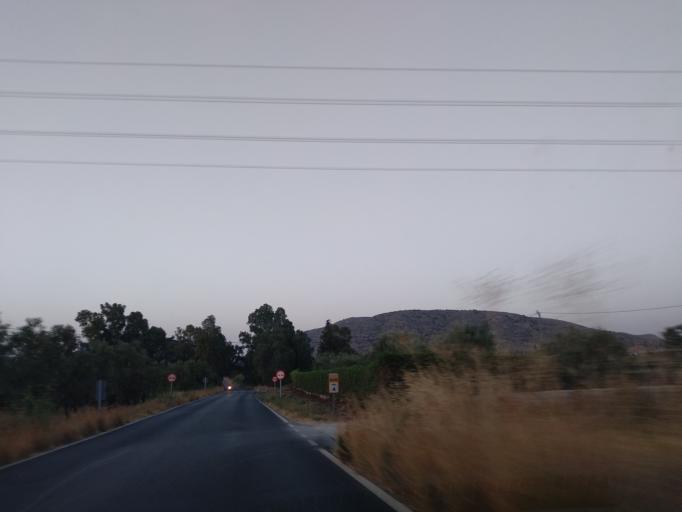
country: ES
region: Andalusia
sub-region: Provincia de Malaga
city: Cartama
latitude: 36.6811
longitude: -4.6567
